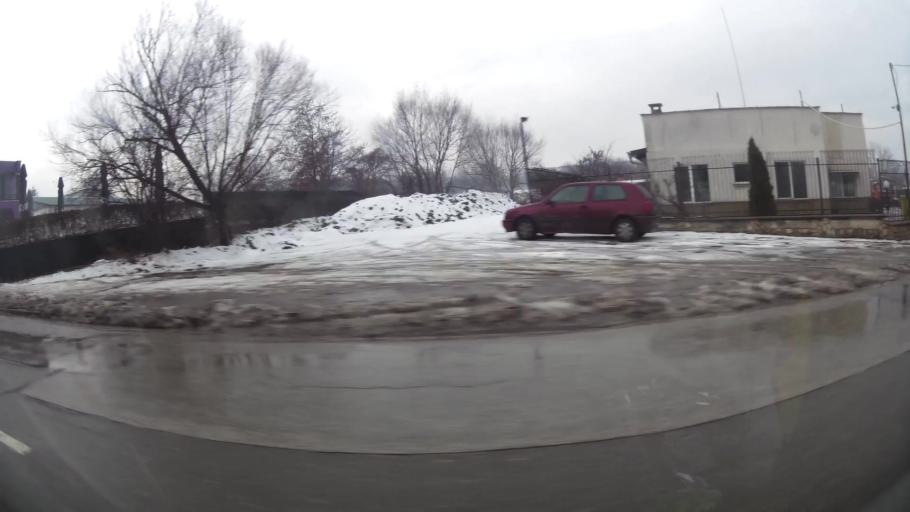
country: BG
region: Sofiya
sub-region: Obshtina Bozhurishte
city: Bozhurishte
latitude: 42.6872
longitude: 23.2399
